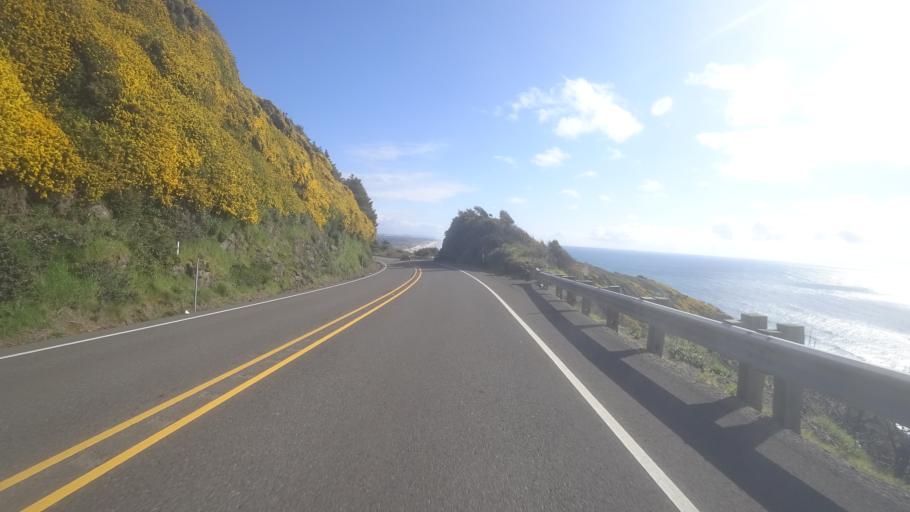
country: US
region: Oregon
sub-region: Lane County
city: Florence
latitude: 44.1115
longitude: -124.1234
